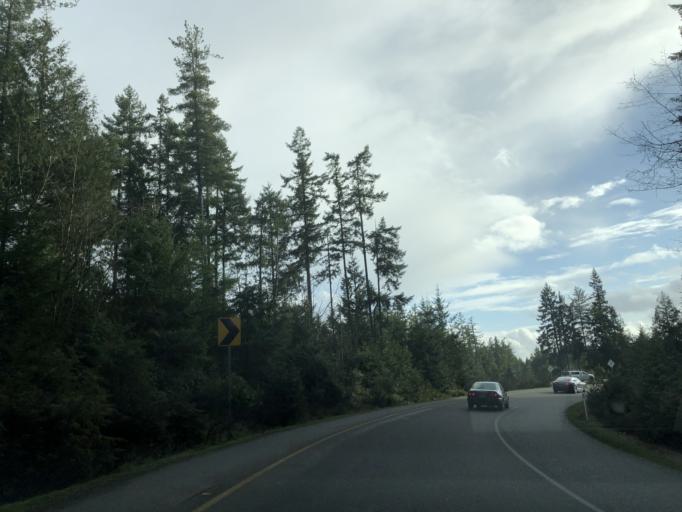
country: US
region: Washington
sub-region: Kitsap County
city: Poulsbo
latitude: 47.7607
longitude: -122.6559
